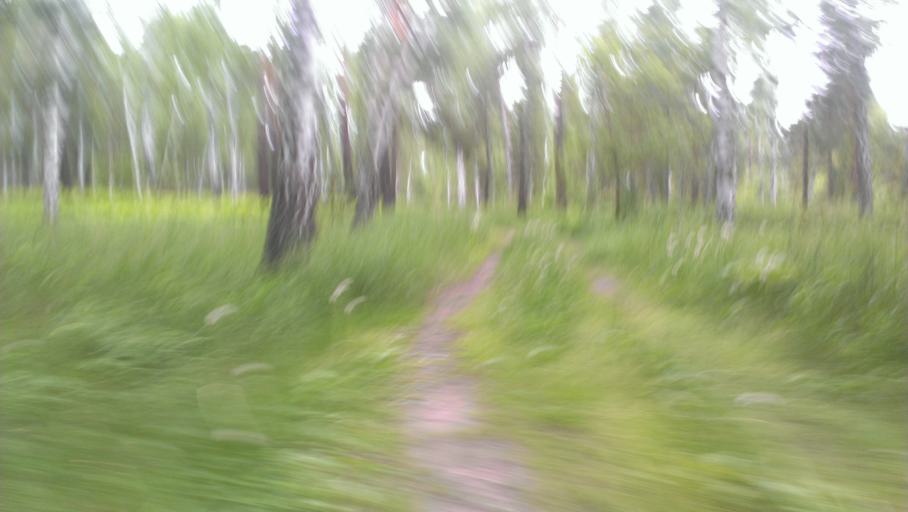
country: RU
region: Altai Krai
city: Sannikovo
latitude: 53.3399
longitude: 84.0488
